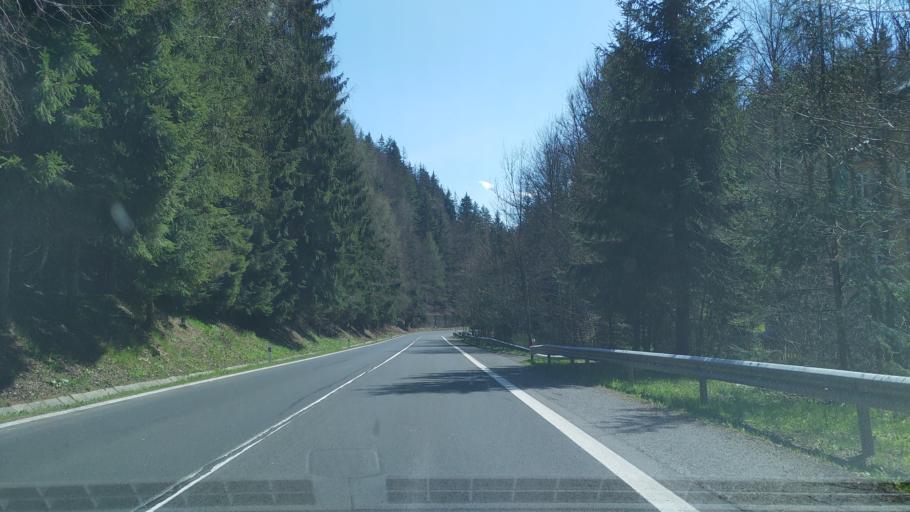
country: CZ
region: Karlovarsky
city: Jachymov
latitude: 50.3535
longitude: 12.9324
